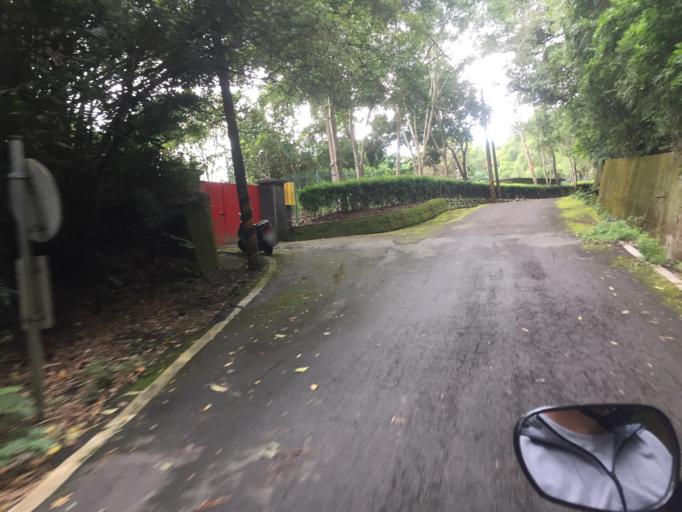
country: TW
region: Taiwan
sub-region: Hsinchu
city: Zhubei
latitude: 24.7864
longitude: 121.1582
